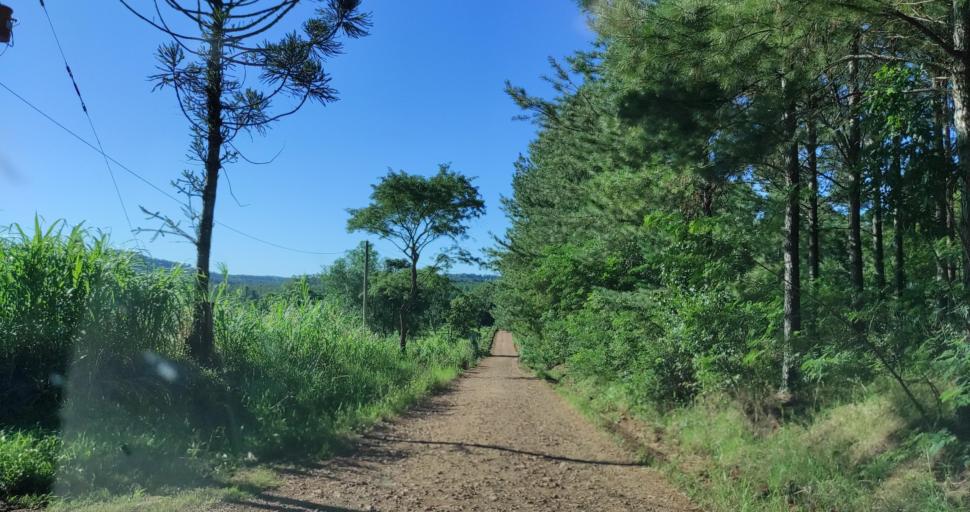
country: AR
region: Misiones
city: Capiovi
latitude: -26.9327
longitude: -55.0014
